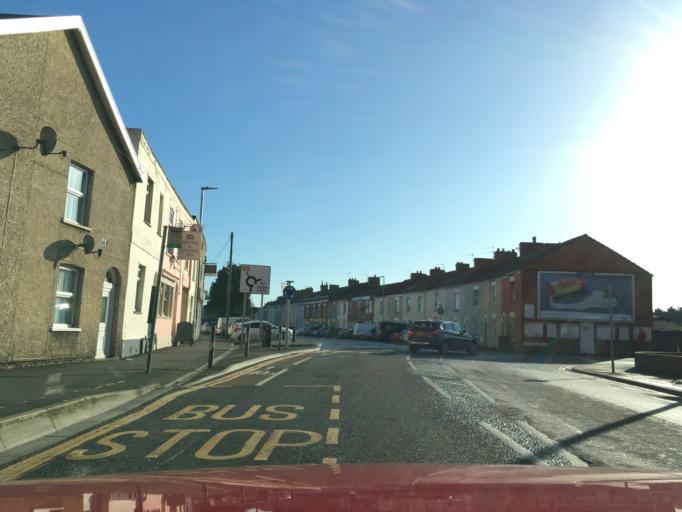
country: GB
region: England
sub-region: Somerset
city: Bridgwater
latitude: 51.1275
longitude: -2.9928
